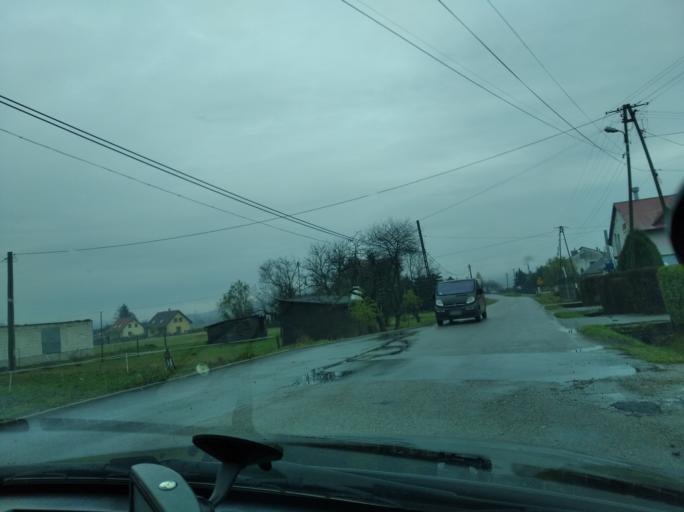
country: PL
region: Subcarpathian Voivodeship
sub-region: Powiat strzyzowski
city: Babica
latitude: 49.9288
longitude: 21.8522
